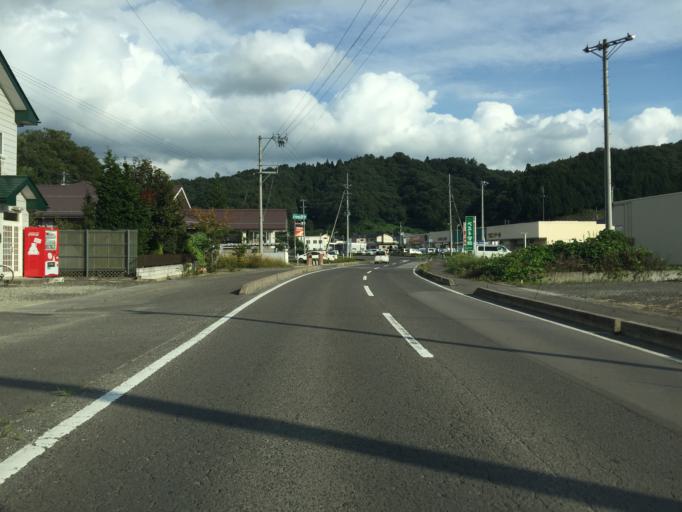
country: JP
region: Fukushima
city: Fukushima-shi
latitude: 37.6665
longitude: 140.5761
